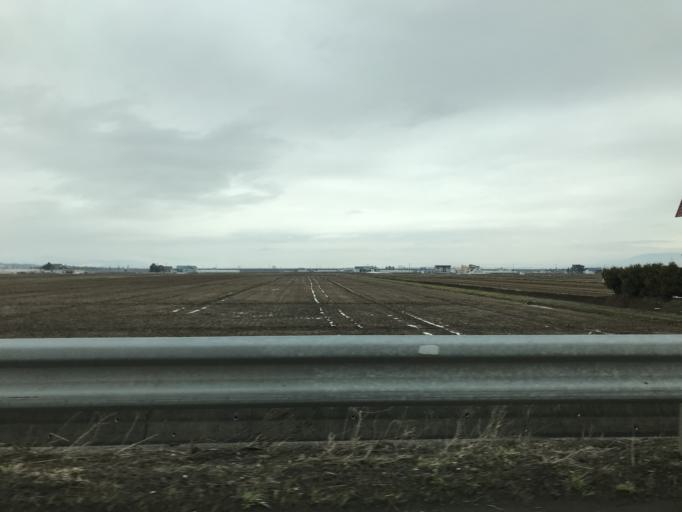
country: JP
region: Hokkaido
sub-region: Asahikawa-shi
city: Asahikawa
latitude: 43.8319
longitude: 142.4258
